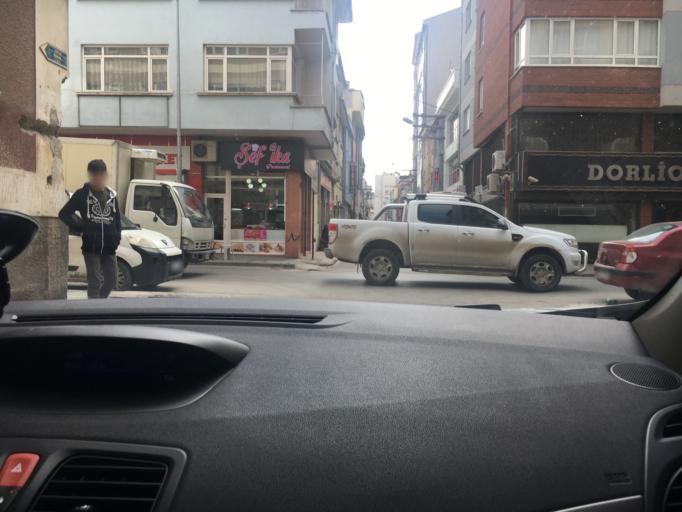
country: TR
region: Eskisehir
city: Eskisehir
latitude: 39.7792
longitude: 30.5169
